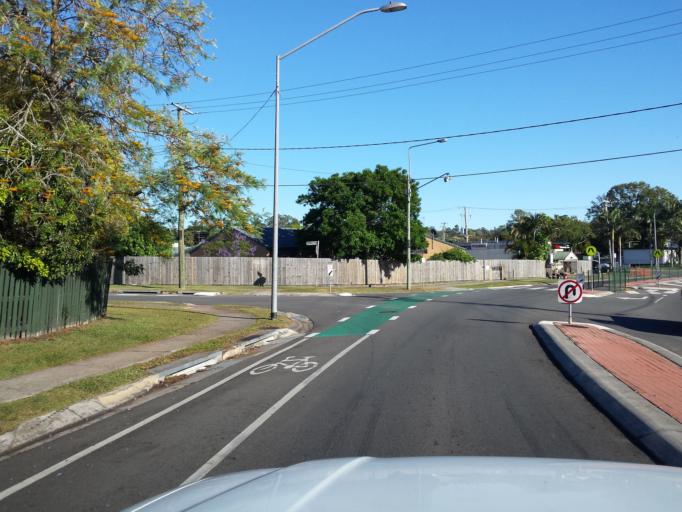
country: AU
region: Queensland
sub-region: Logan
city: Logan City
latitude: -27.6543
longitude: 153.1106
